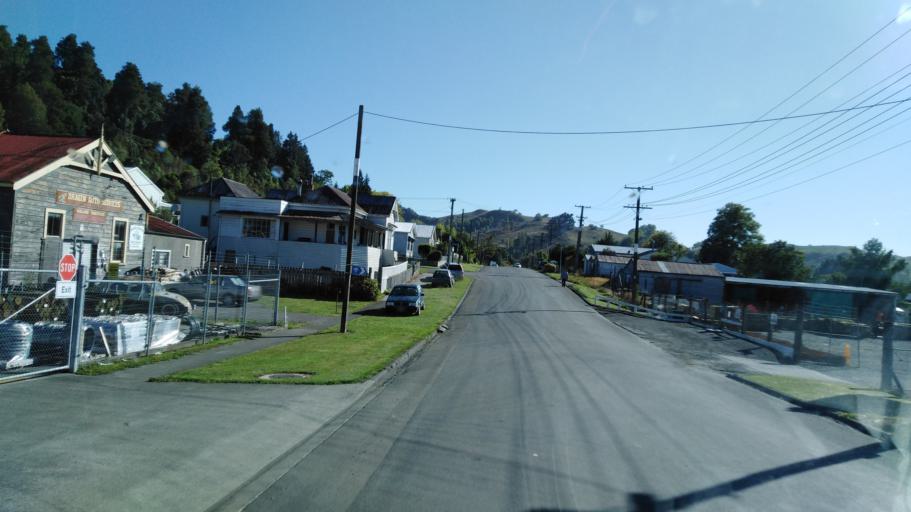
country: NZ
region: Manawatu-Wanganui
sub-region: Ruapehu District
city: Waiouru
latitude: -39.6751
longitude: 175.7973
